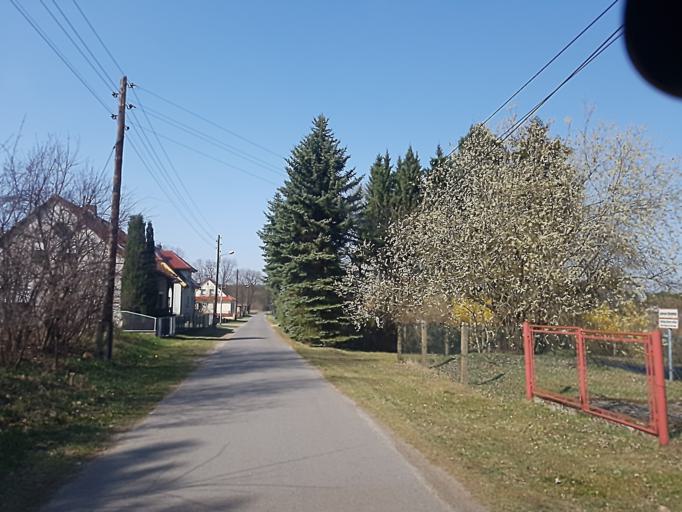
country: DE
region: Brandenburg
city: Tschernitz
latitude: 51.6556
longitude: 14.5765
